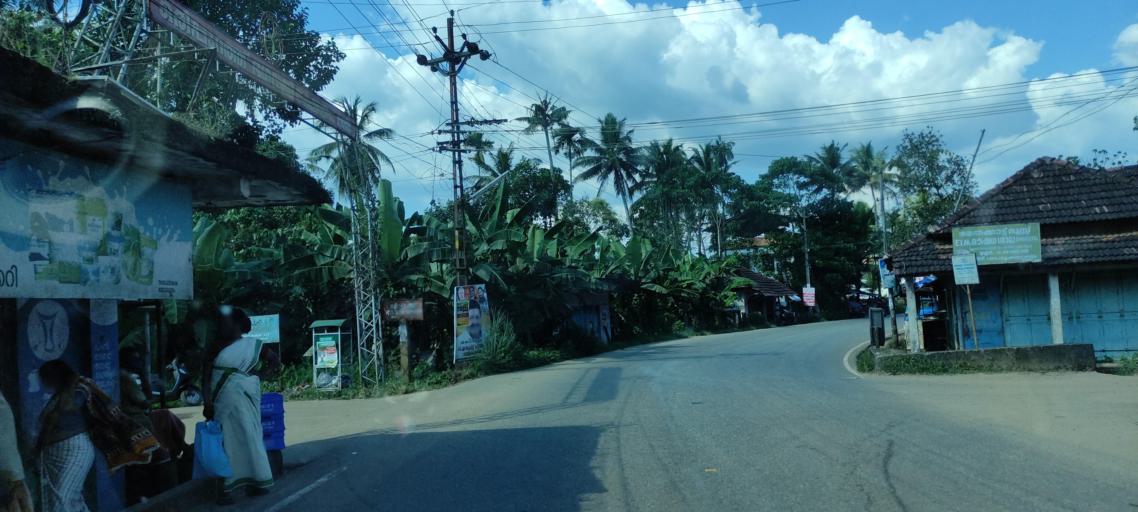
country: IN
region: Kerala
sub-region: Pattanamtitta
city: Adur
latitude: 9.2091
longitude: 76.7461
